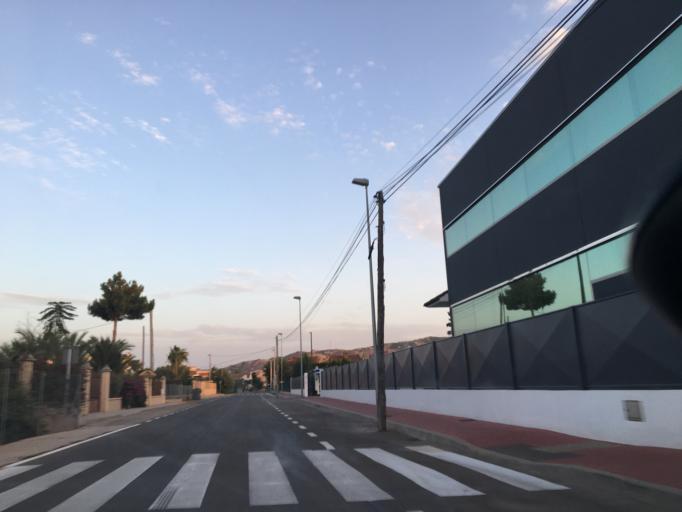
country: ES
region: Murcia
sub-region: Murcia
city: Santomera
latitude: 38.0199
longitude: -1.0528
